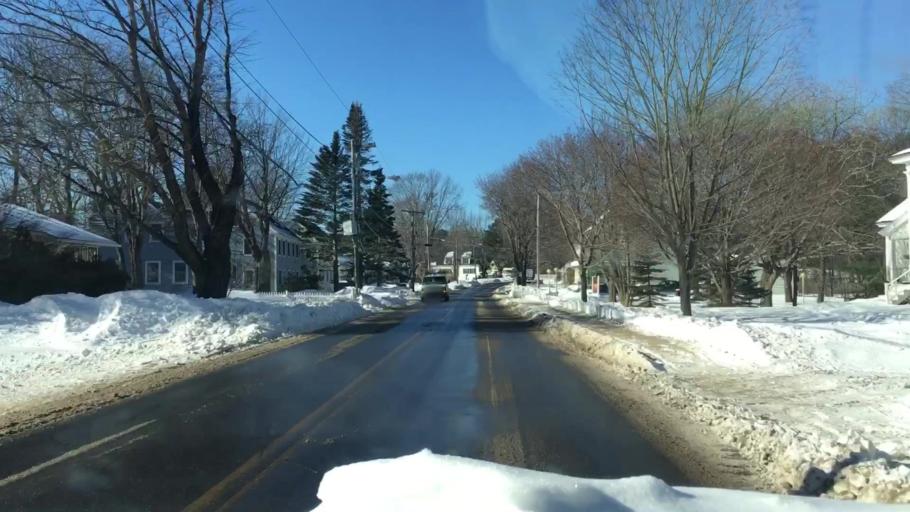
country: US
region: Maine
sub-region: Sagadahoc County
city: Topsham
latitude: 43.9250
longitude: -69.9672
